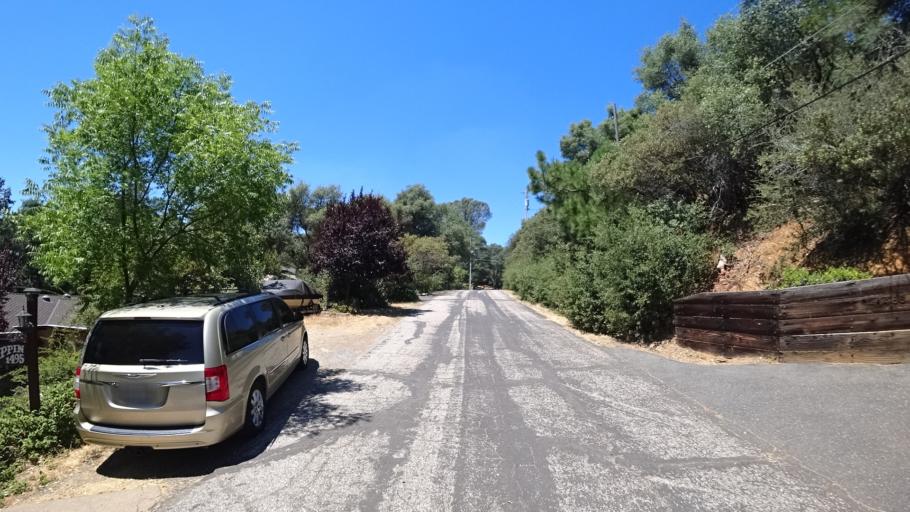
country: US
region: California
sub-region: Calaveras County
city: Murphys
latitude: 38.1340
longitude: -120.4402
